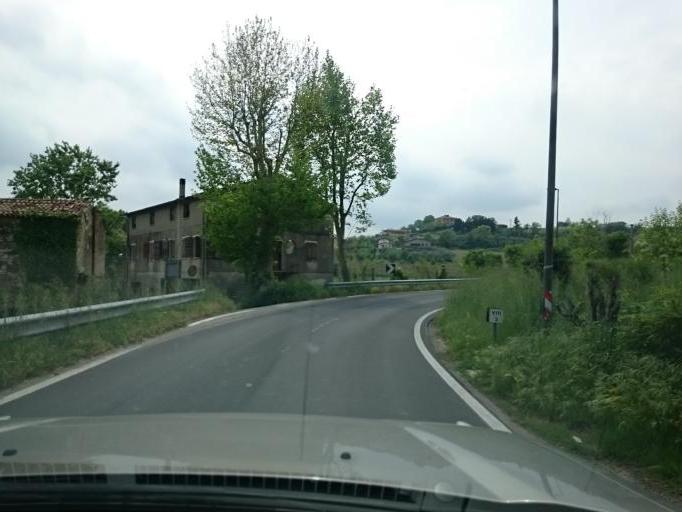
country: IT
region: Veneto
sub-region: Provincia di Padova
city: Arqua Petrarca
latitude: 45.2694
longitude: 11.7321
